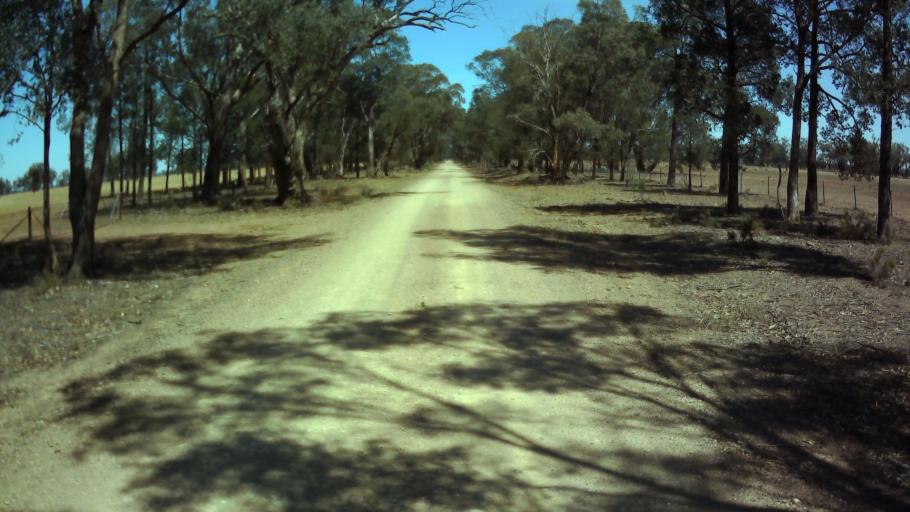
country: AU
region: New South Wales
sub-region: Weddin
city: Grenfell
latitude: -34.0695
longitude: 147.9000
